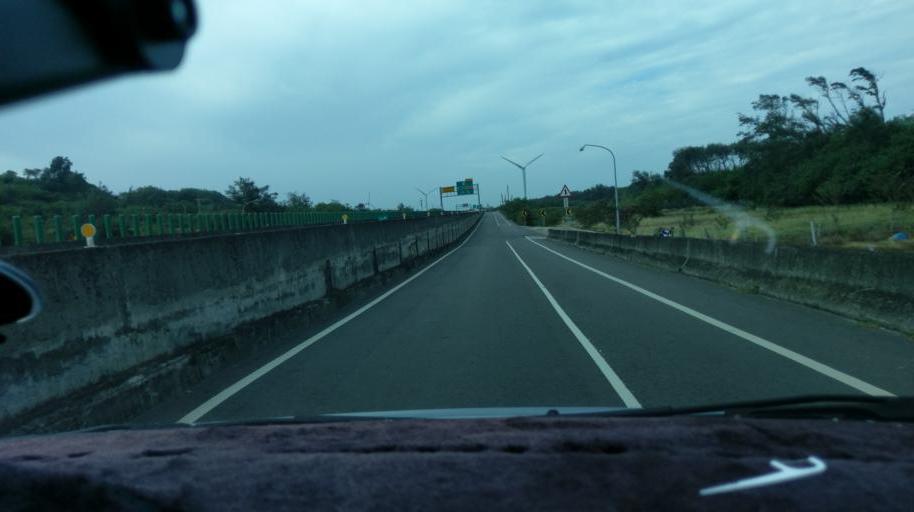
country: TW
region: Taiwan
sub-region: Hsinchu
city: Hsinchu
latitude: 24.7305
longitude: 120.8768
